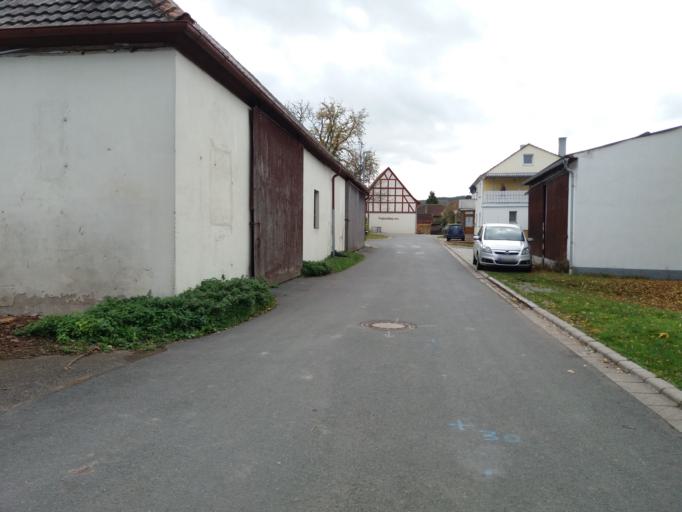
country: DE
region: Bavaria
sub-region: Regierungsbezirk Mittelfranken
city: Illesheim
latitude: 49.4595
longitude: 10.4129
